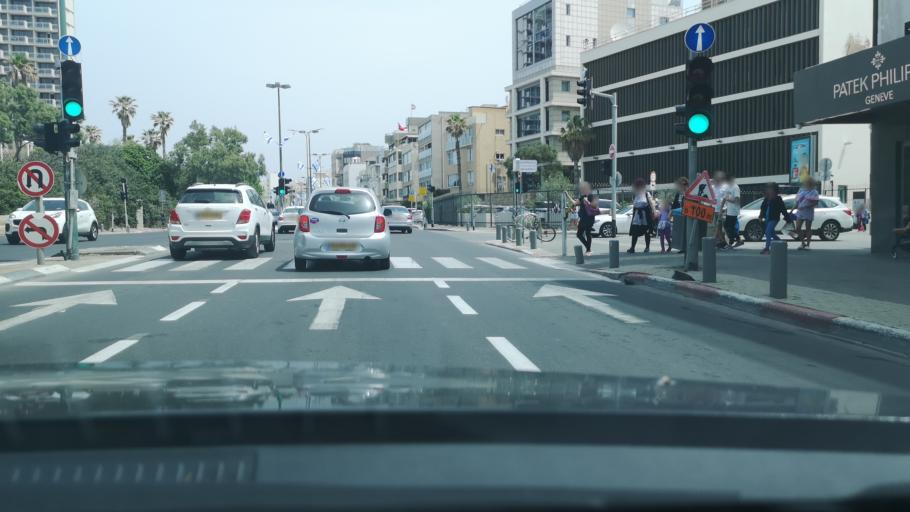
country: IL
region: Tel Aviv
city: Tel Aviv
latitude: 32.0876
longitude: 34.7709
